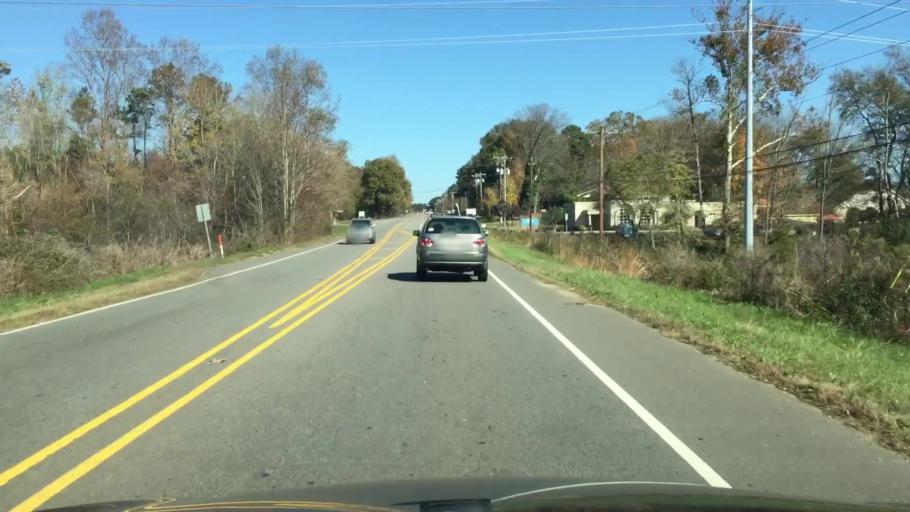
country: US
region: North Carolina
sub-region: Iredell County
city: Mooresville
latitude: 35.5692
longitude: -80.8457
